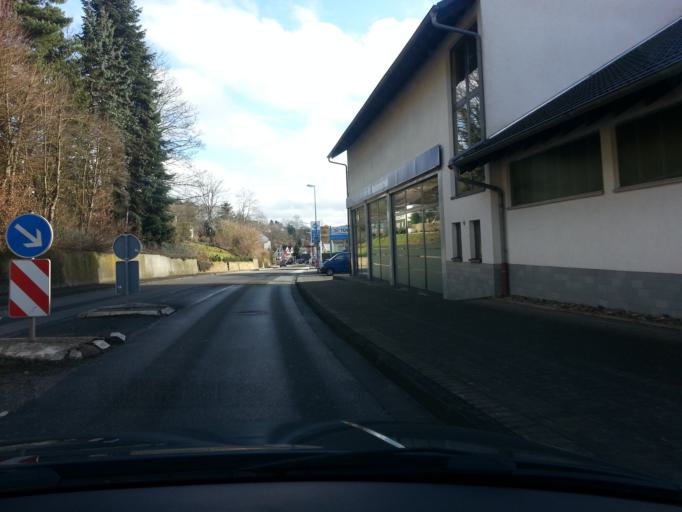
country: DE
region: Rheinland-Pfalz
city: Hochspeyer
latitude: 49.4433
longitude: 7.8817
